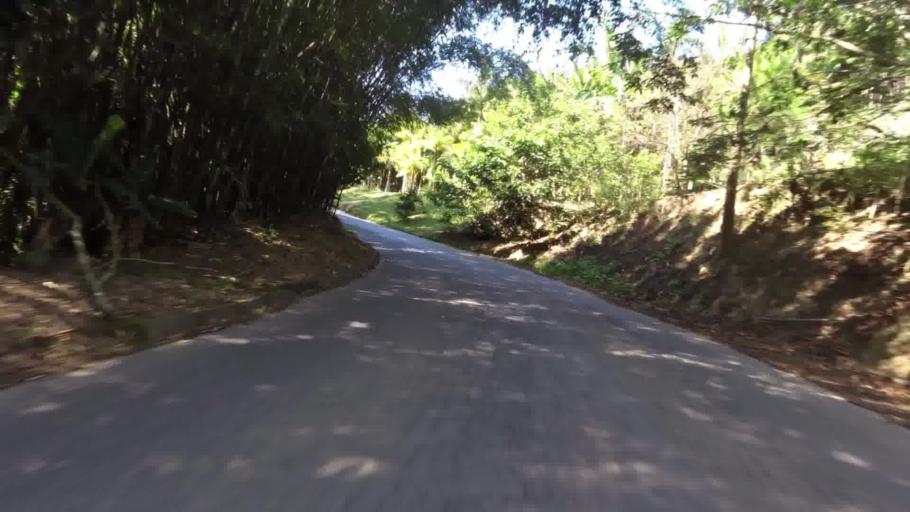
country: BR
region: Espirito Santo
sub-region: Marechal Floriano
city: Marechal Floriano
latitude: -20.4579
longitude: -40.9116
